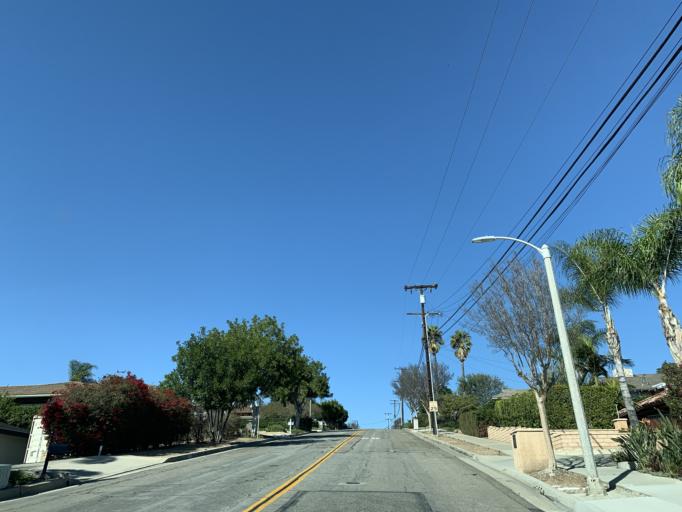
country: US
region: California
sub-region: Orange County
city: Brea
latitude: 33.8869
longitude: -117.8985
